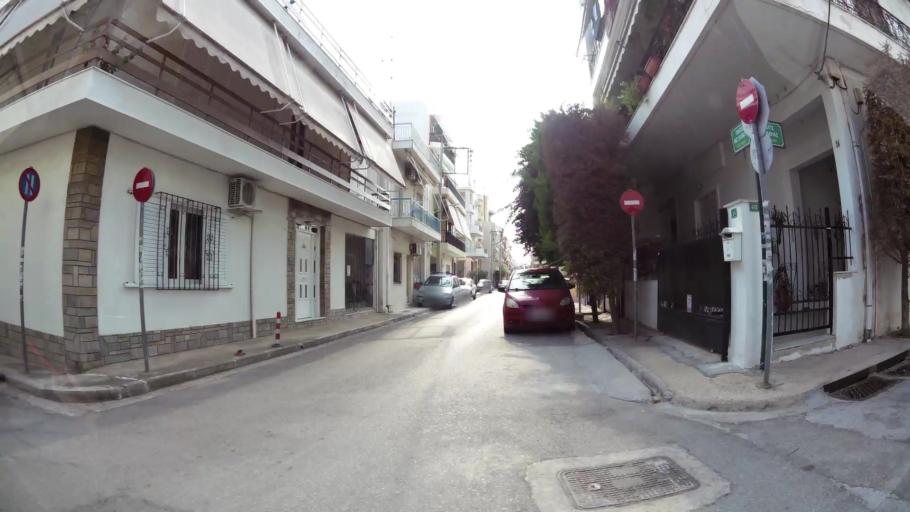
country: GR
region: Attica
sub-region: Nomarchia Athinas
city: Ilion
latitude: 38.0398
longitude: 23.6955
